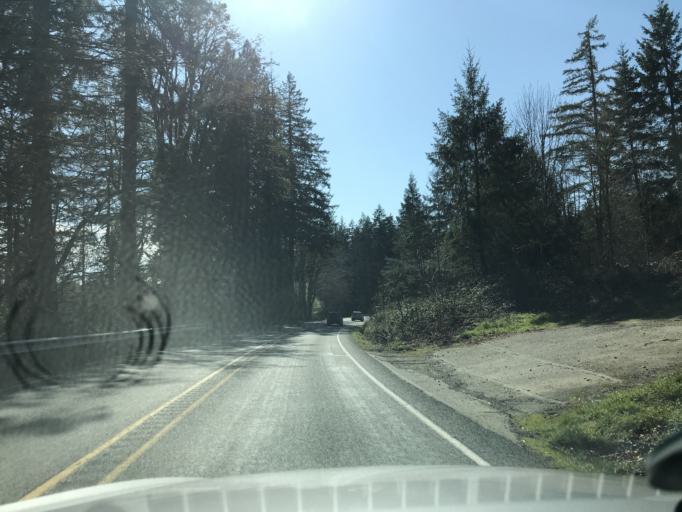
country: US
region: Washington
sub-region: Pierce County
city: Key Center
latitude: 47.3499
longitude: -122.7374
